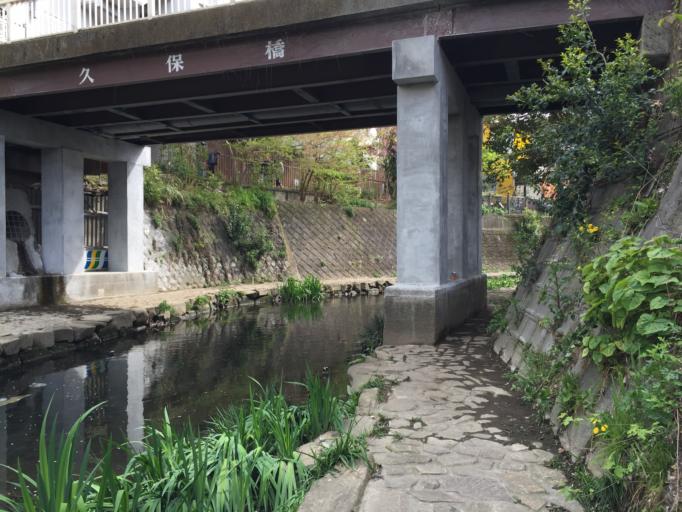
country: JP
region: Kanagawa
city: Yokohama
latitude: 35.4089
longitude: 139.5946
